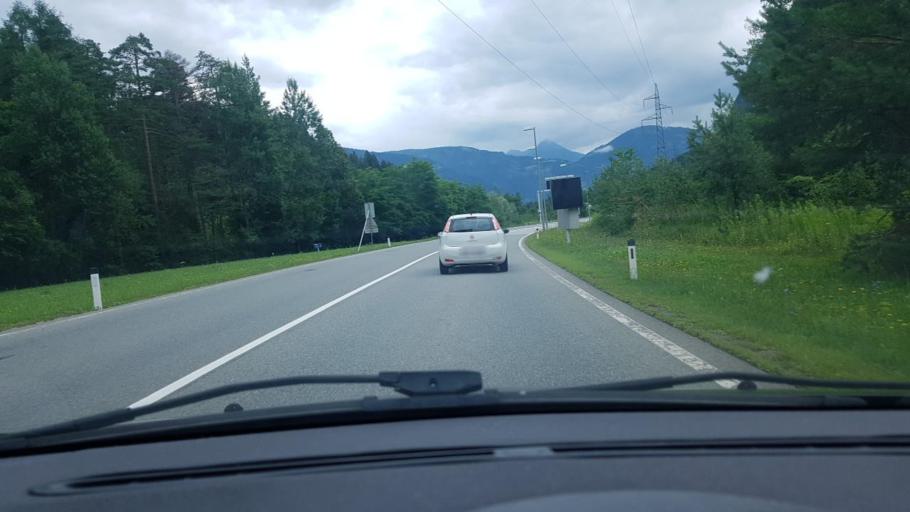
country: AT
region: Tyrol
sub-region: Politischer Bezirk Lienz
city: Leisach
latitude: 46.7990
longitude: 12.7363
